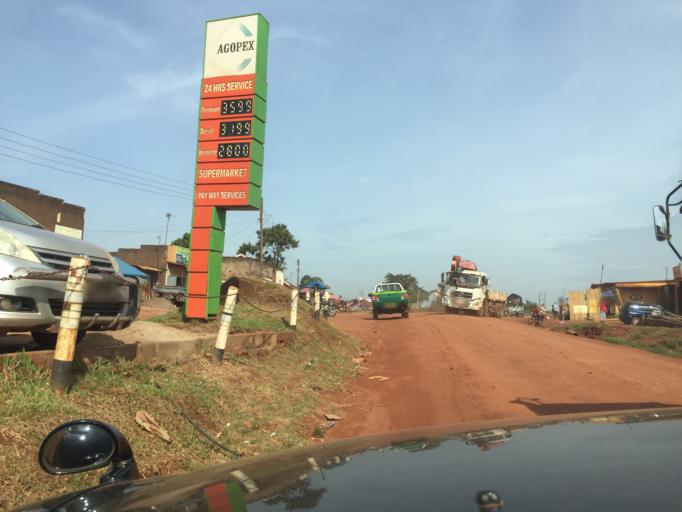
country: UG
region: Central Region
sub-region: Wakiso District
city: Wakiso
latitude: 0.4634
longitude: 32.5550
